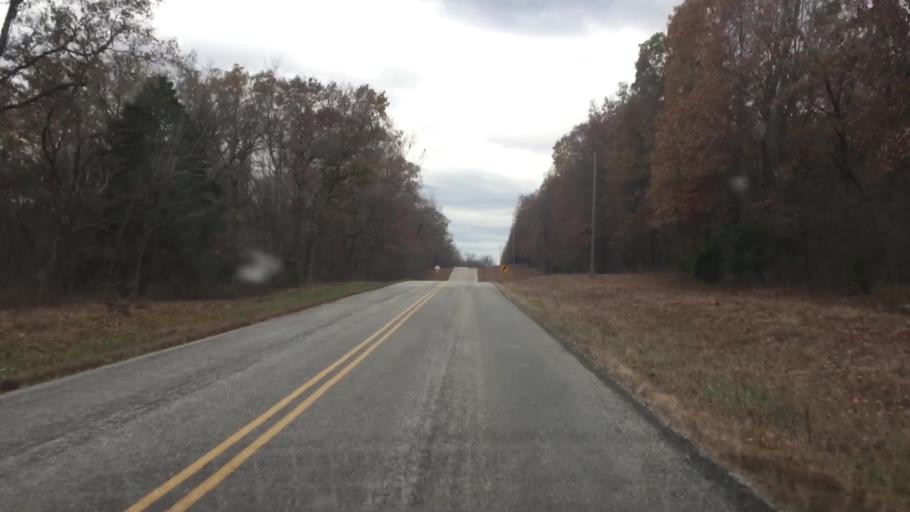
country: US
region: Missouri
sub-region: Saint Clair County
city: Osceola
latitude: 37.9891
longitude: -93.6315
